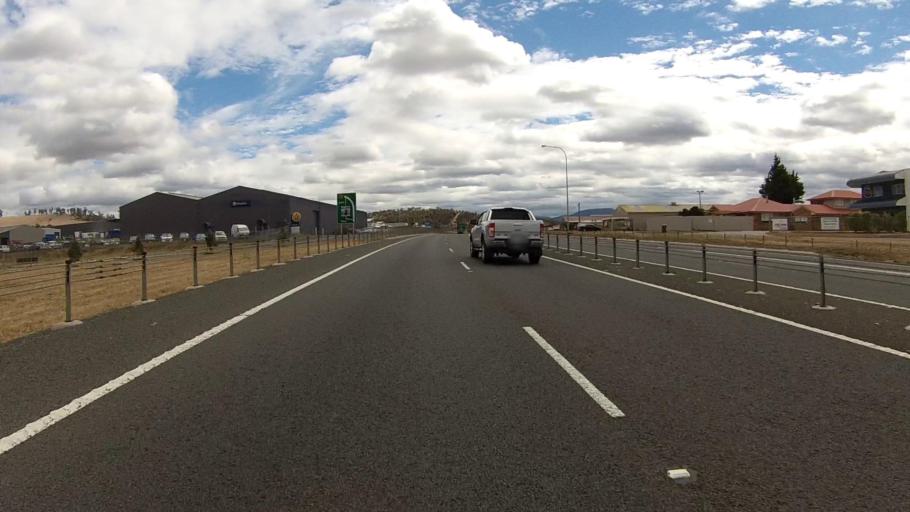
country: AU
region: Tasmania
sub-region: Brighton
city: Bridgewater
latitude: -42.7229
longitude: 147.2371
